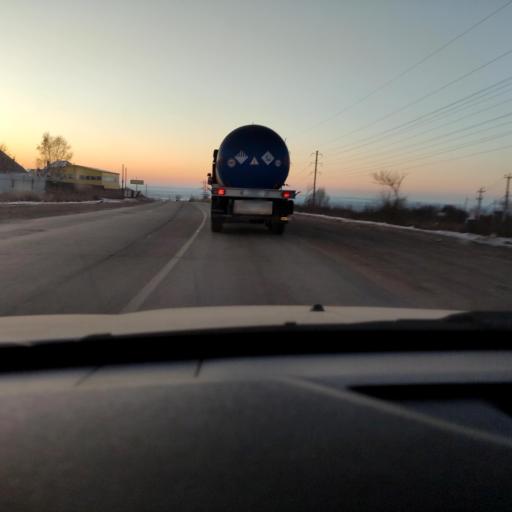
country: RU
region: Samara
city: Smyshlyayevka
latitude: 53.2488
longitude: 50.4749
